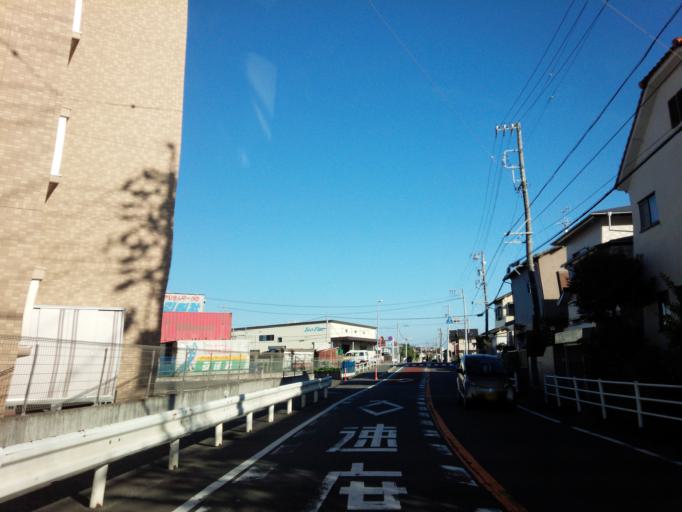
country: JP
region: Shizuoka
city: Shizuoka-shi
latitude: 34.9446
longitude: 138.4075
